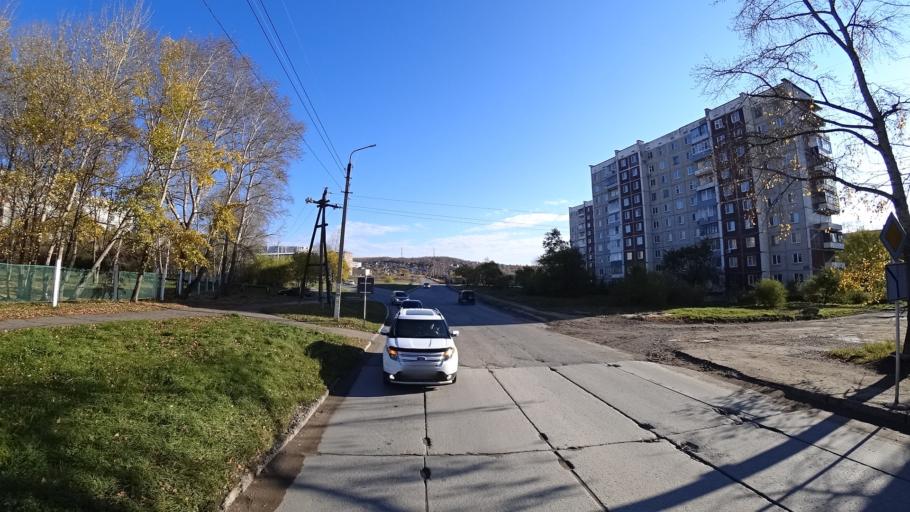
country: RU
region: Khabarovsk Krai
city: Amursk
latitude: 50.2335
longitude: 136.9095
